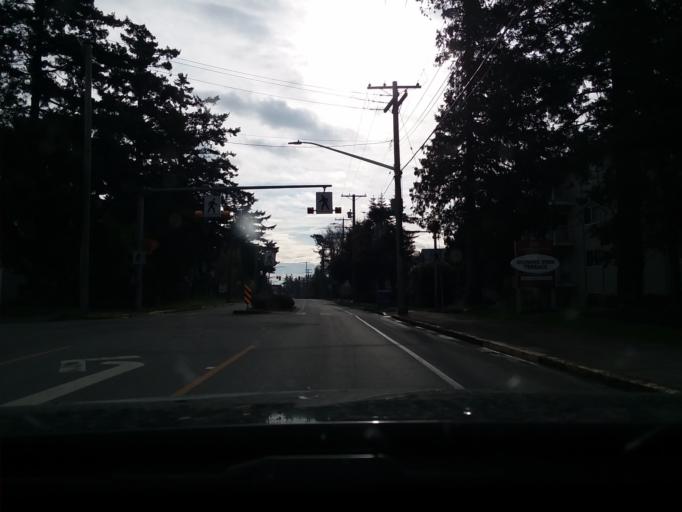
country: CA
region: British Columbia
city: Victoria
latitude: 48.4406
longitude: -123.3984
